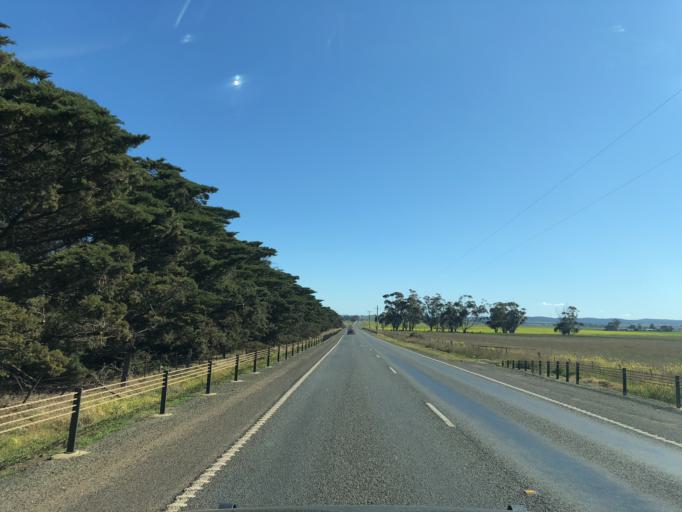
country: AU
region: Victoria
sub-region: Hume
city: Diggers Rest
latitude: -37.6282
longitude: 144.6977
